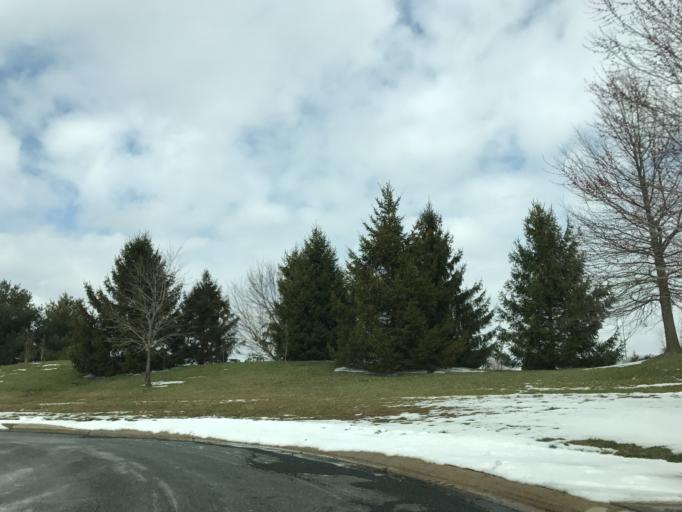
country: US
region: Maryland
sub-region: Harford County
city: Bel Air North
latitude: 39.5754
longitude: -76.3798
